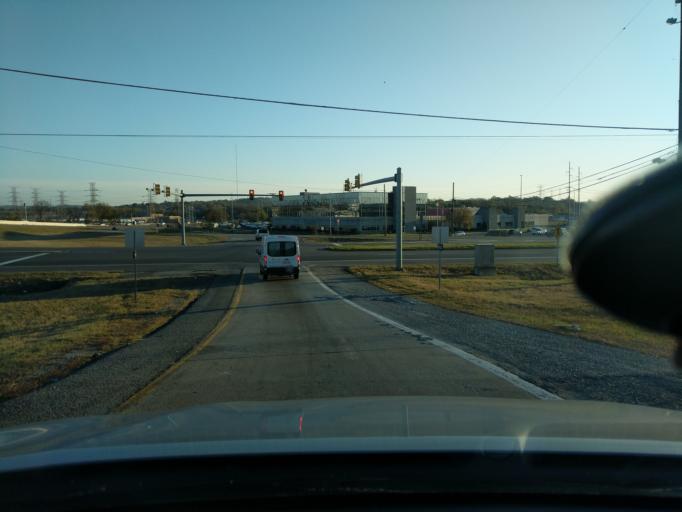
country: US
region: Tennessee
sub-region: Davidson County
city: Belle Meade
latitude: 36.1717
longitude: -86.8704
